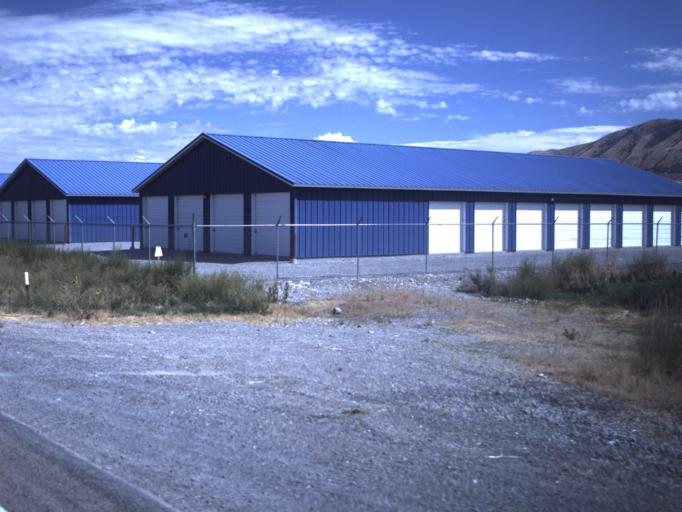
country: US
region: Utah
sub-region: Box Elder County
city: Elwood
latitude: 41.7073
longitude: -112.1421
